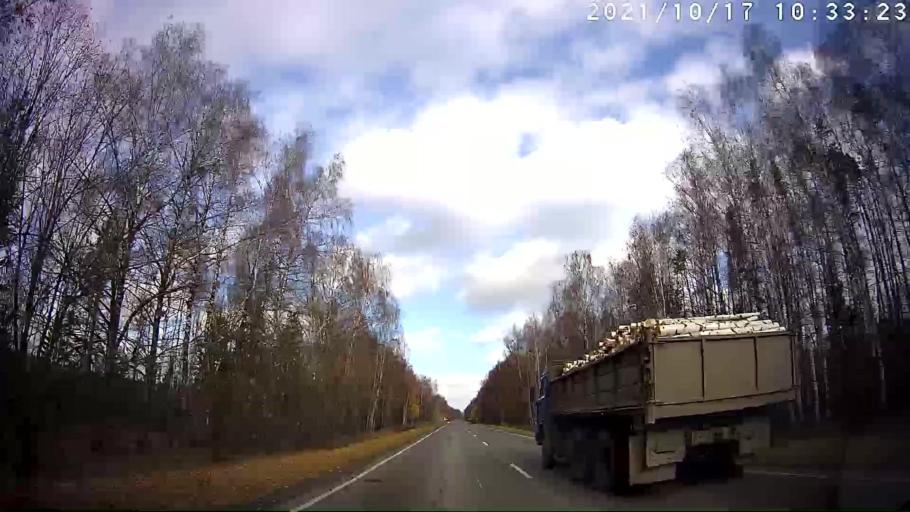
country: RU
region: Mariy-El
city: Kuzhener
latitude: 56.9088
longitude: 48.7542
